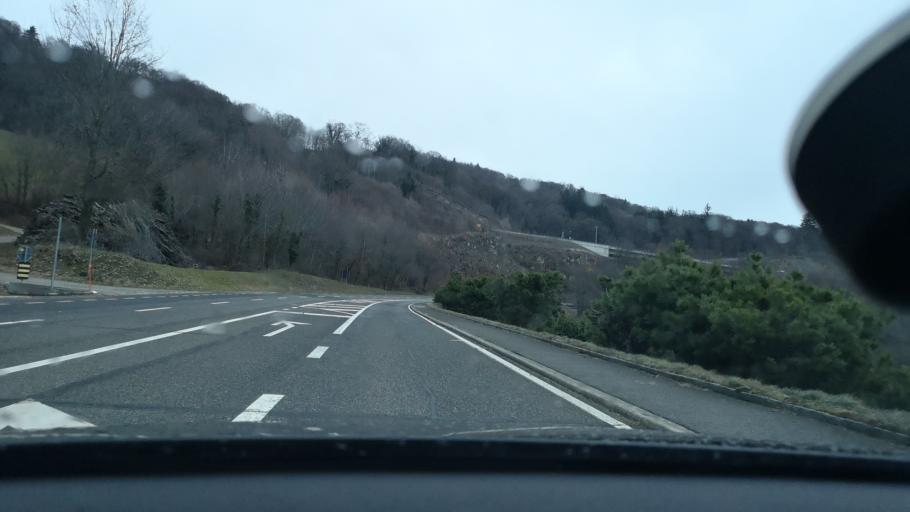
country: CH
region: Neuchatel
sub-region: Boudry District
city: Saint-Aubin-Sauges
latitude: 46.8587
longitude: 6.7300
